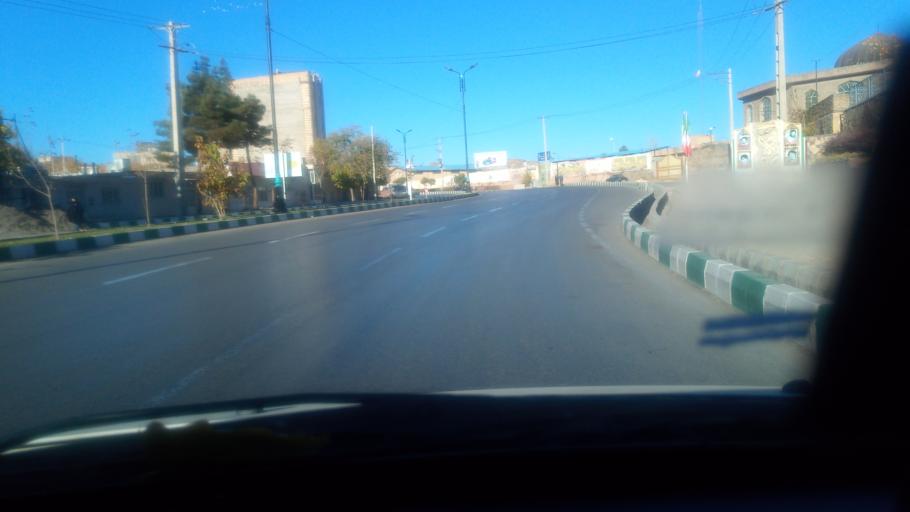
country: IR
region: Razavi Khorasan
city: Torqabeh
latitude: 36.3139
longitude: 59.3736
